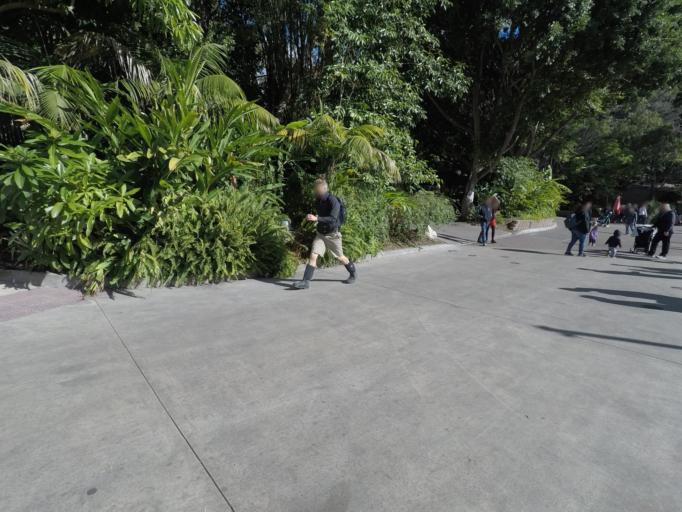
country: US
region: California
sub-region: San Diego County
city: San Diego
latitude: 32.7360
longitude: -117.1519
